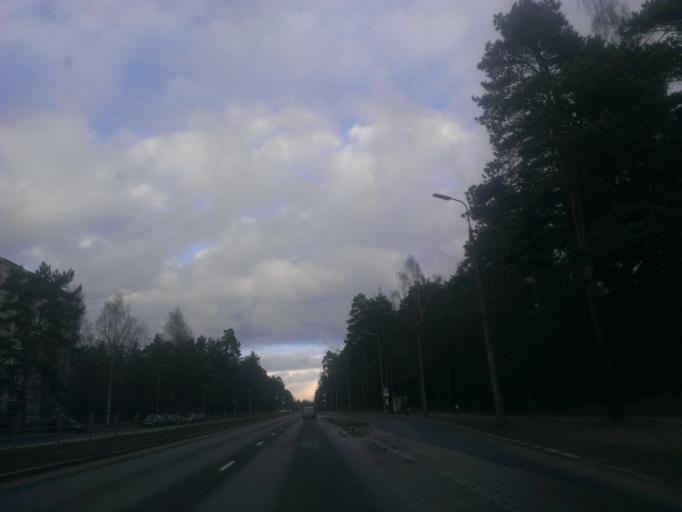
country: LV
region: Riga
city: Jaunciems
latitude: 57.0089
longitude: 24.1292
